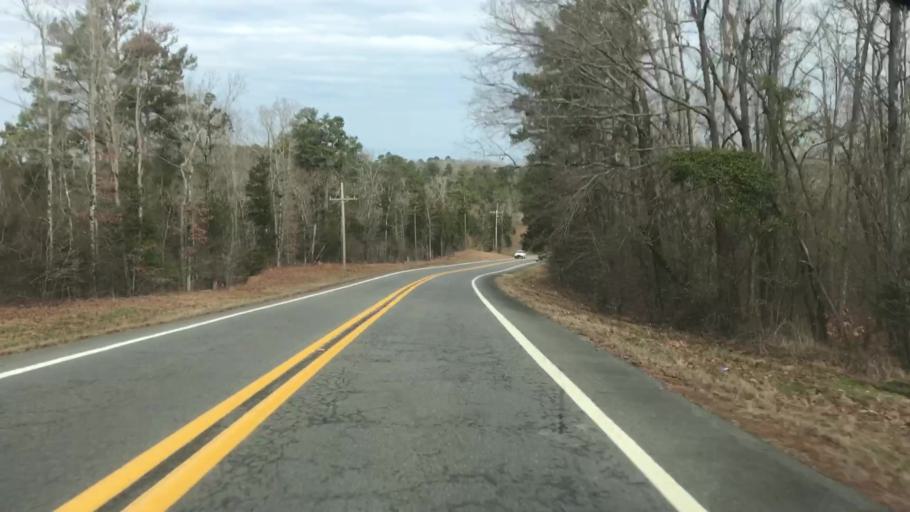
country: US
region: Arkansas
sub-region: Montgomery County
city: Mount Ida
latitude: 34.6163
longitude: -93.7034
